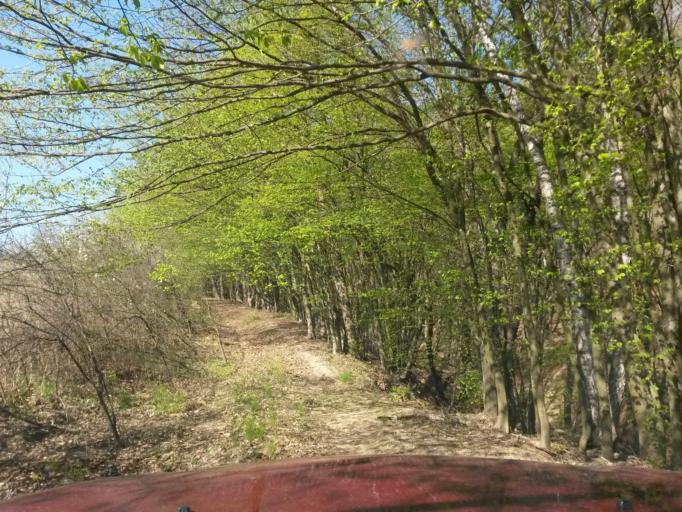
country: SK
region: Presovsky
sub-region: Okres Presov
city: Presov
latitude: 48.9644
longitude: 21.1111
